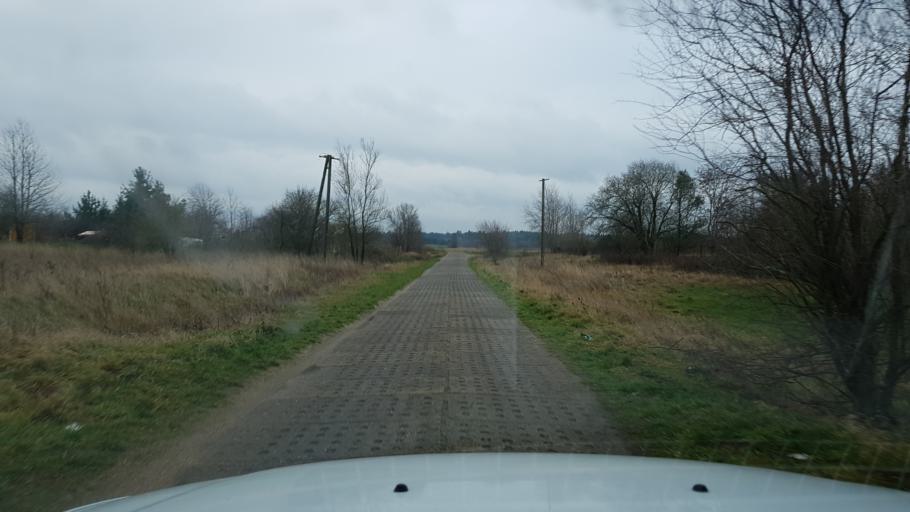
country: PL
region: West Pomeranian Voivodeship
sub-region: Powiat kolobrzeski
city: Grzybowo
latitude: 54.0896
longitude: 15.4282
